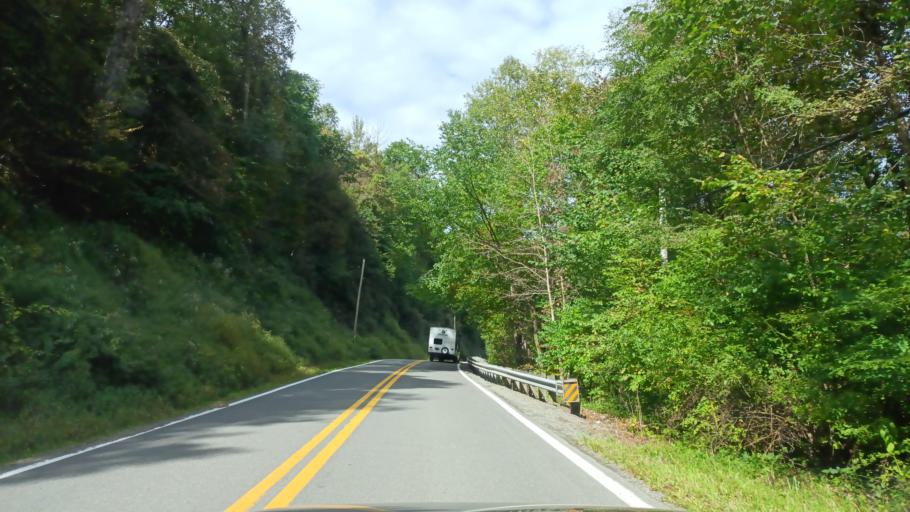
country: US
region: West Virginia
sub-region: Preston County
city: Kingwood
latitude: 39.3230
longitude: -79.6618
